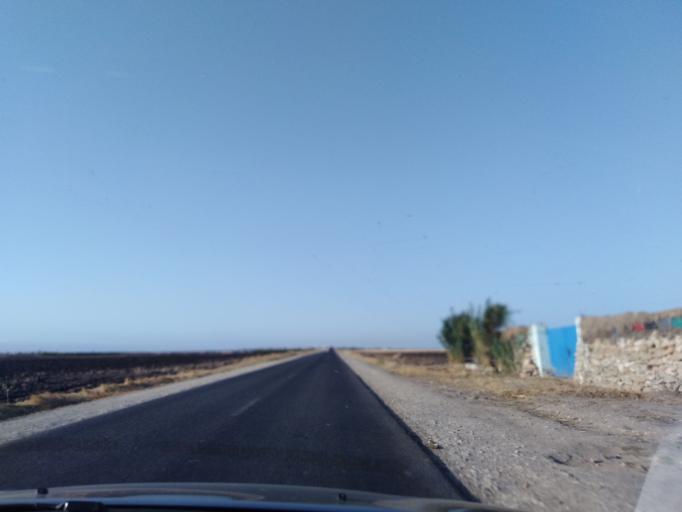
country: MA
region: Doukkala-Abda
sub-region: Safi
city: Safi
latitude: 32.5108
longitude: -8.9175
